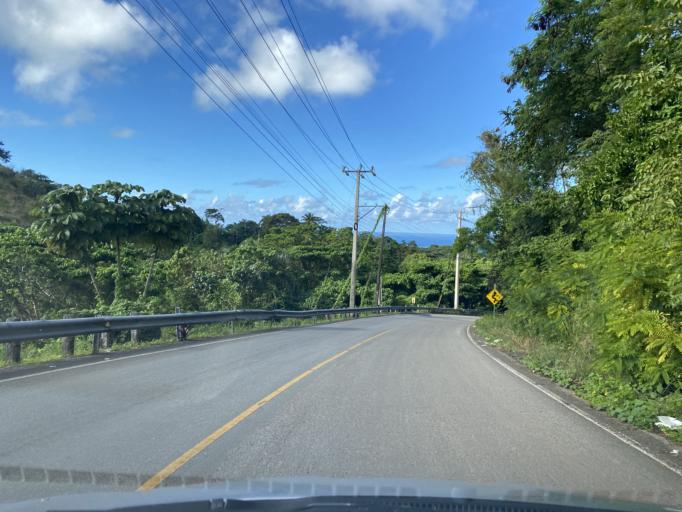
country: DO
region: Samana
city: Las Terrenas
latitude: 19.2862
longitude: -69.5526
